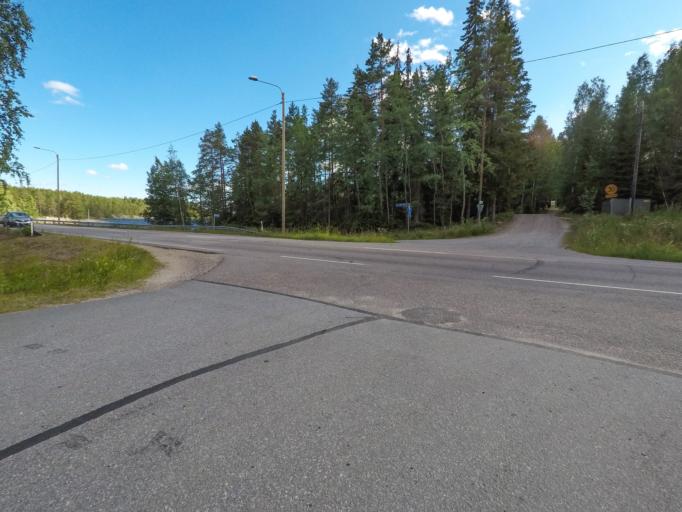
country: FI
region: South Karelia
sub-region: Lappeenranta
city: Lappeenranta
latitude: 61.1008
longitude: 28.1288
